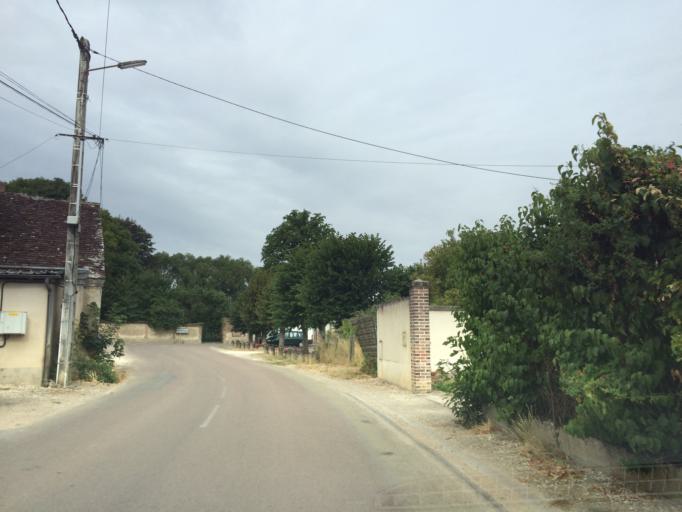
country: FR
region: Bourgogne
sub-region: Departement de l'Yonne
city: Aillant-sur-Tholon
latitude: 47.8523
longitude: 3.3497
